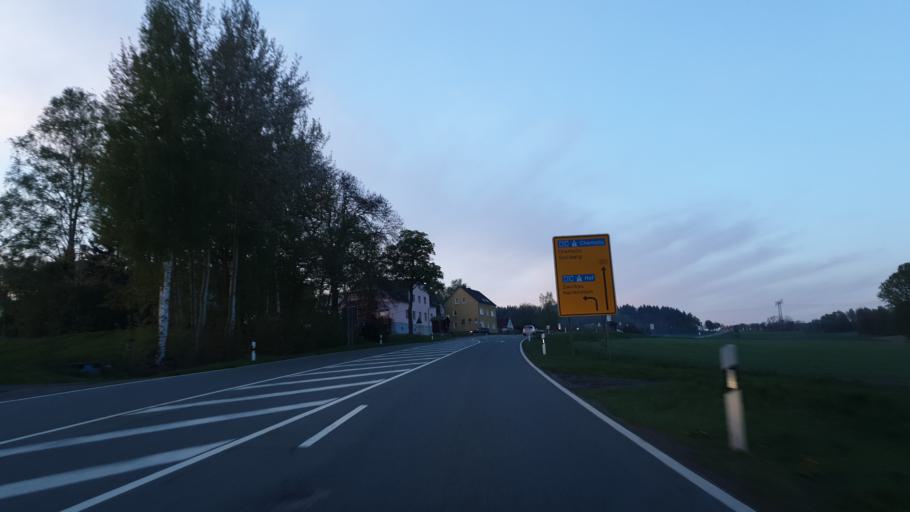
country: DE
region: Saxony
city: Lossnitz
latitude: 50.6392
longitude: 12.7347
